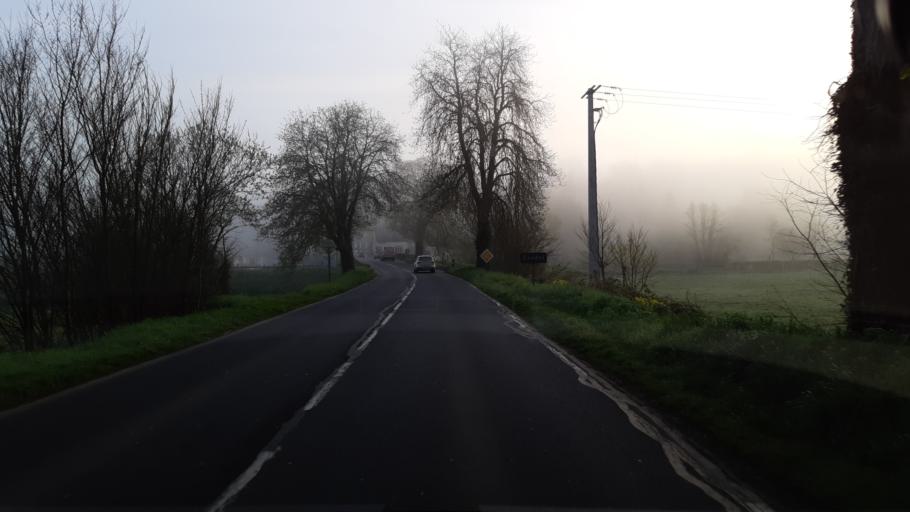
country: FR
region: Lower Normandy
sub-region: Departement de la Manche
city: Agneaux
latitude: 49.0905
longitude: -1.1187
